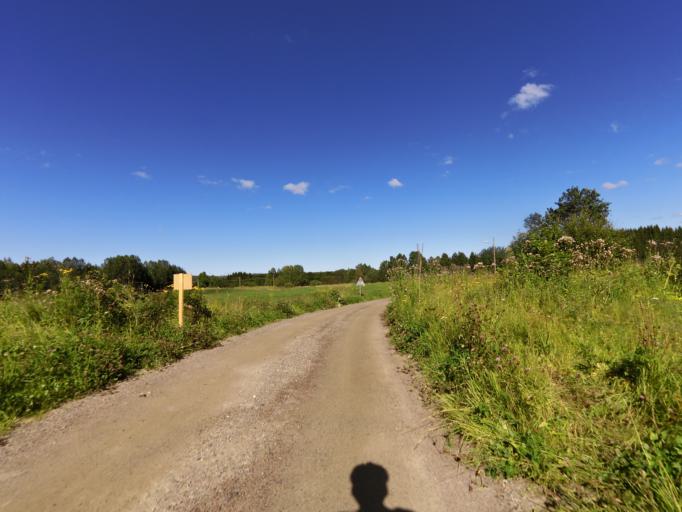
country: SE
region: Gaevleborg
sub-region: Hofors Kommun
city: Hofors
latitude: 60.5137
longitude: 16.4148
